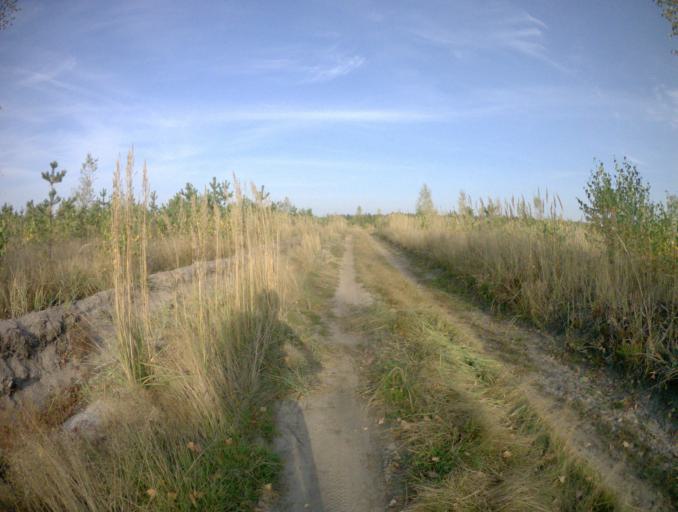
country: RU
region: Vladimir
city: Sobinka
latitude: 55.9784
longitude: 40.0634
